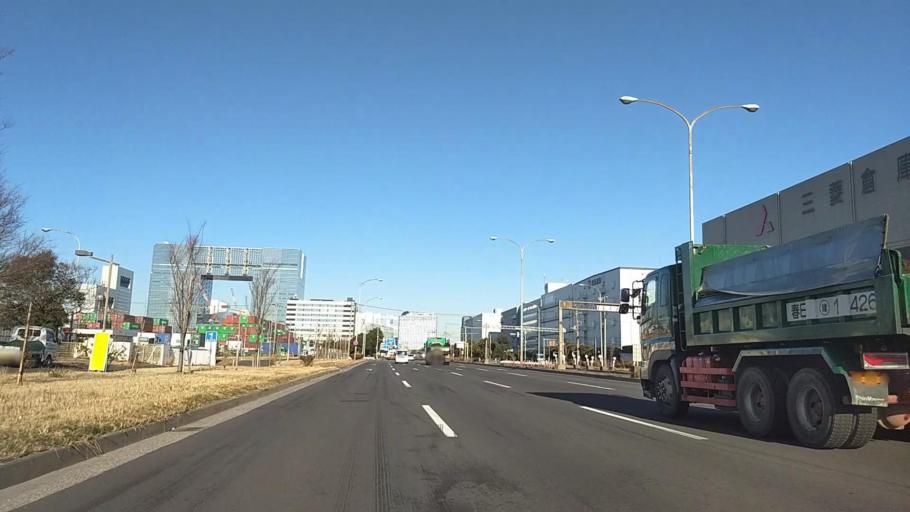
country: JP
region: Kanagawa
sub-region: Kawasaki-shi
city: Kawasaki
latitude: 35.6127
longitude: 139.7855
